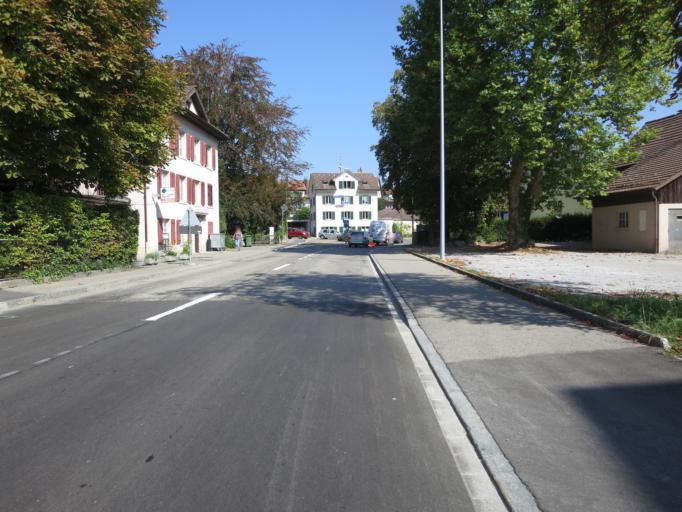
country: CH
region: Zurich
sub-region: Bezirk Meilen
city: Hombrechtikon
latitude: 47.2531
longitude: 8.7802
